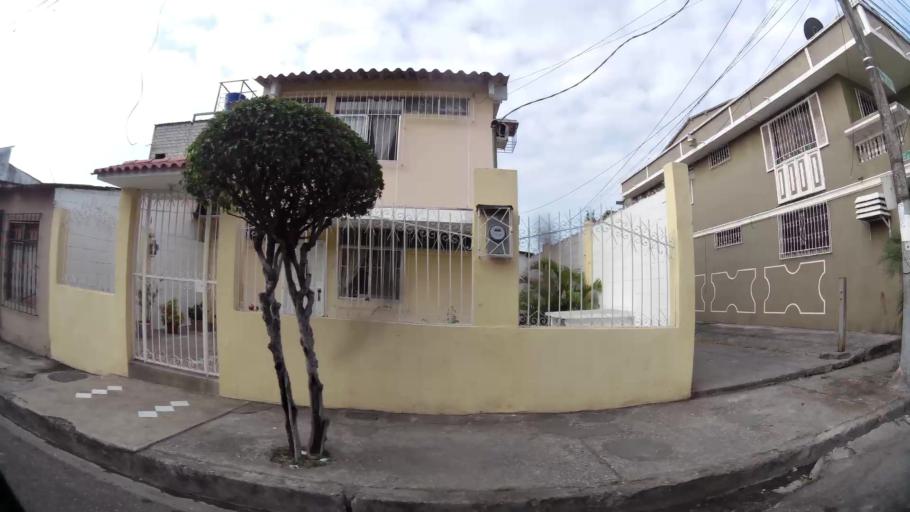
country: EC
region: Guayas
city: Eloy Alfaro
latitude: -2.1302
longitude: -79.8948
